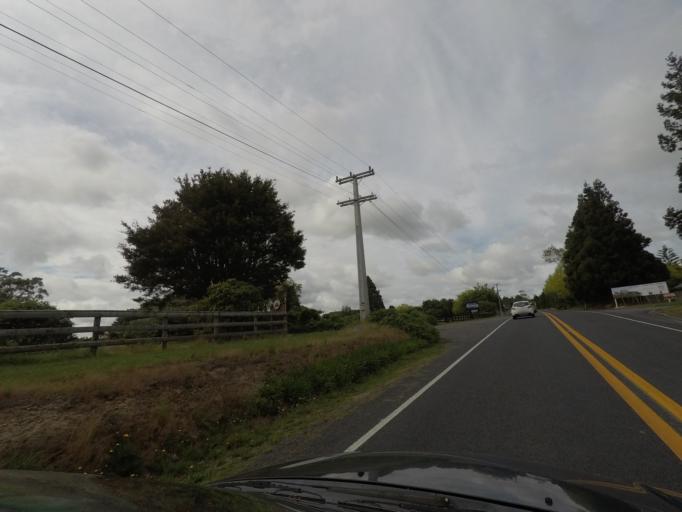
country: NZ
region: Auckland
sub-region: Auckland
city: Rosebank
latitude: -36.7720
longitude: 174.5874
